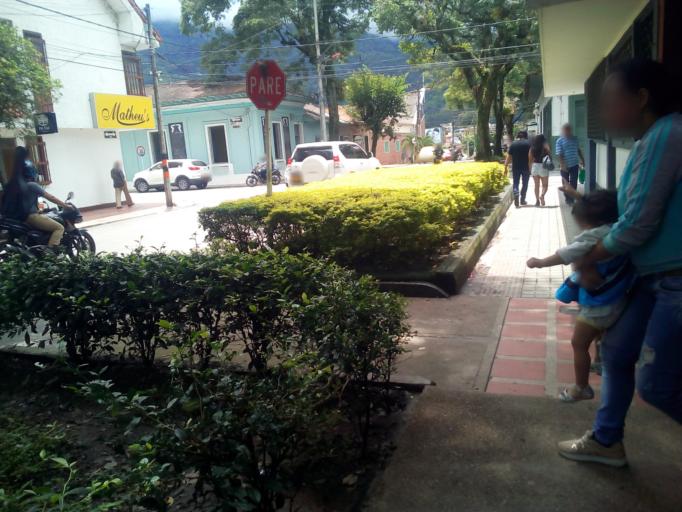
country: CO
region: Tolima
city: Ibague
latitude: 4.4463
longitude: -75.2449
